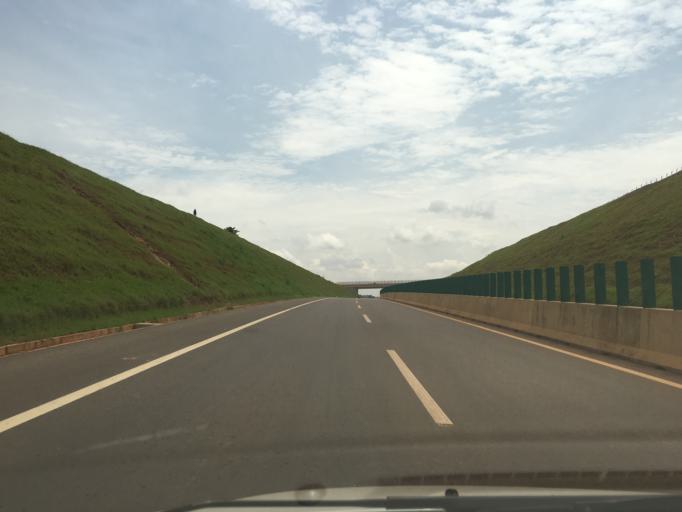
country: UG
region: Central Region
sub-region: Wakiso District
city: Kajansi
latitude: 0.1735
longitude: 32.5158
